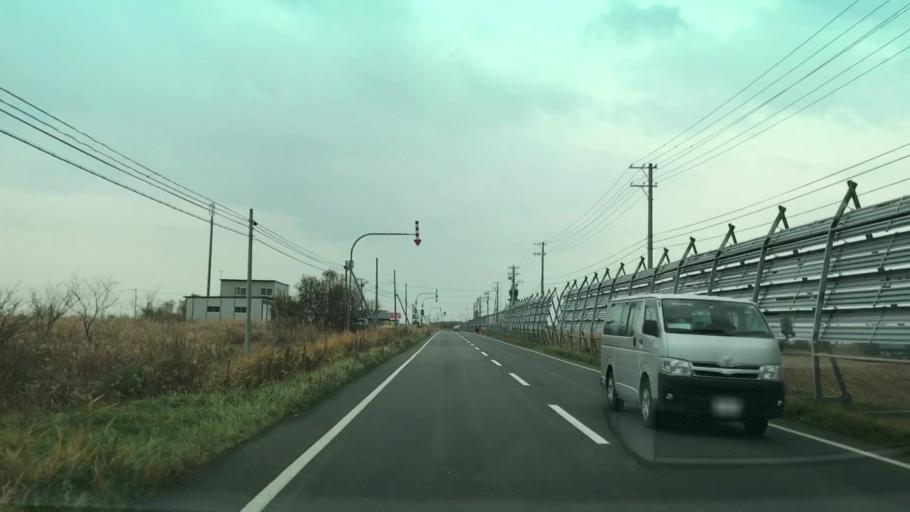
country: JP
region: Hokkaido
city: Ishikari
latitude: 43.2843
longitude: 141.4099
